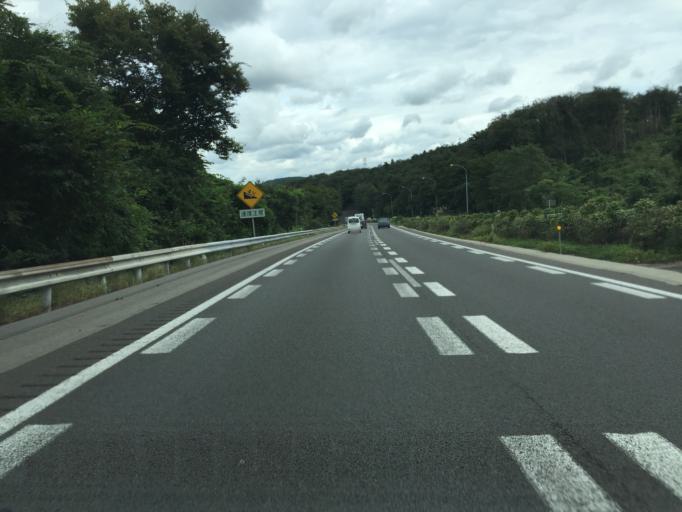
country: JP
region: Miyagi
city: Shiroishi
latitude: 37.9457
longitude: 140.6133
